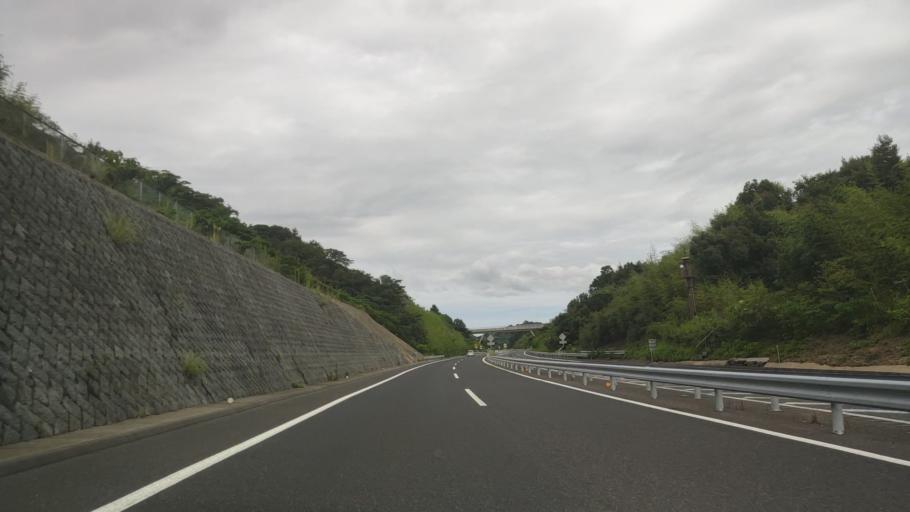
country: JP
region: Wakayama
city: Tanabe
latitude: 33.7590
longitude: 135.3536
